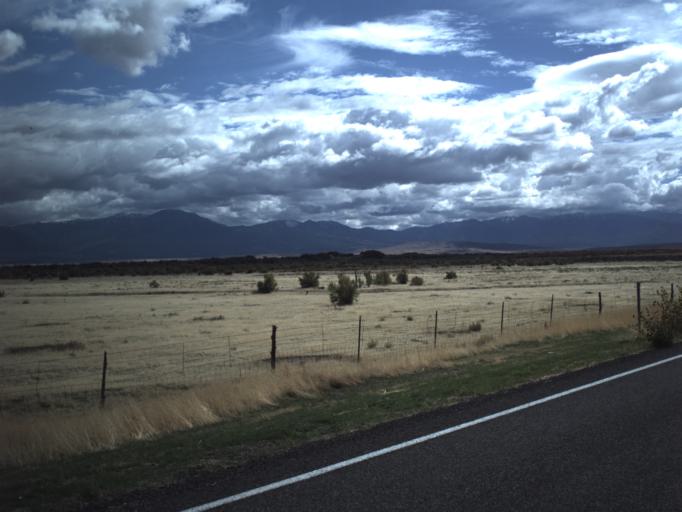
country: US
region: Utah
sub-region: Millard County
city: Fillmore
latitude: 39.1429
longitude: -112.4098
